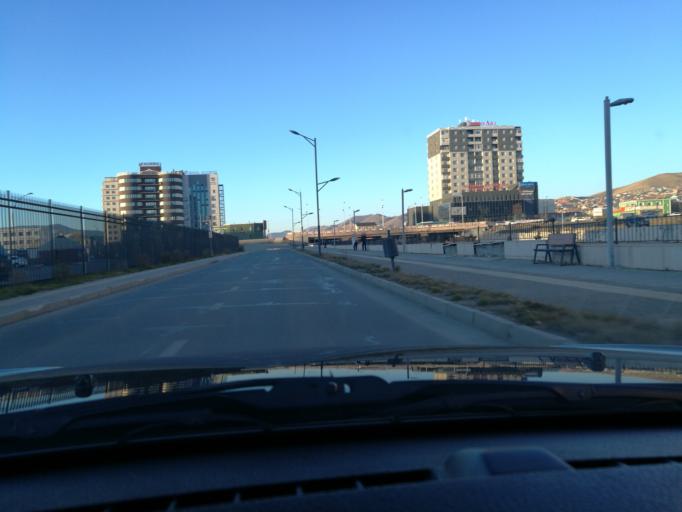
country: MN
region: Ulaanbaatar
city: Ulaanbaatar
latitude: 47.9279
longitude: 106.9314
